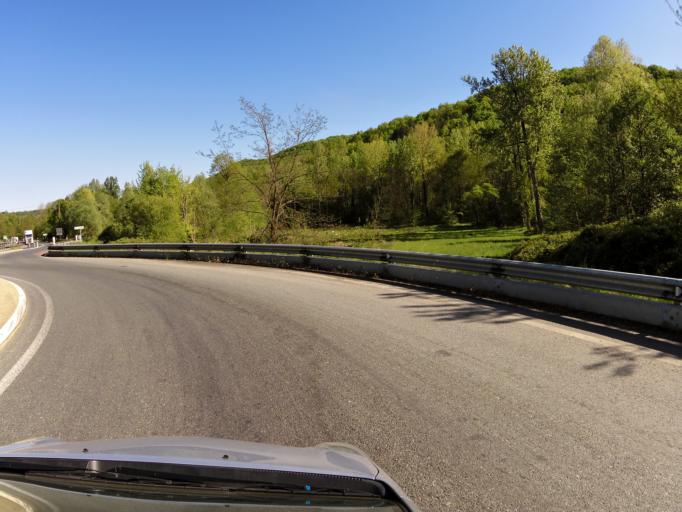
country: FR
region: Aquitaine
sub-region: Departement de la Dordogne
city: Montignac
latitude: 45.1482
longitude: 1.1716
